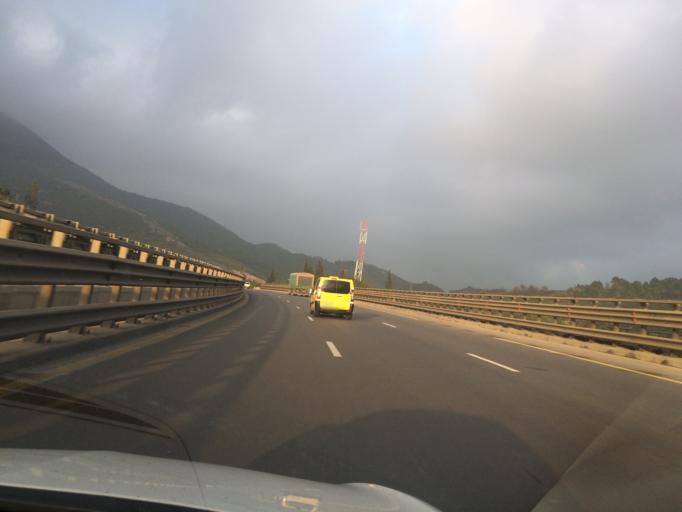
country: DZ
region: Tipaza
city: El Affroun
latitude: 36.3973
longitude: 2.5368
